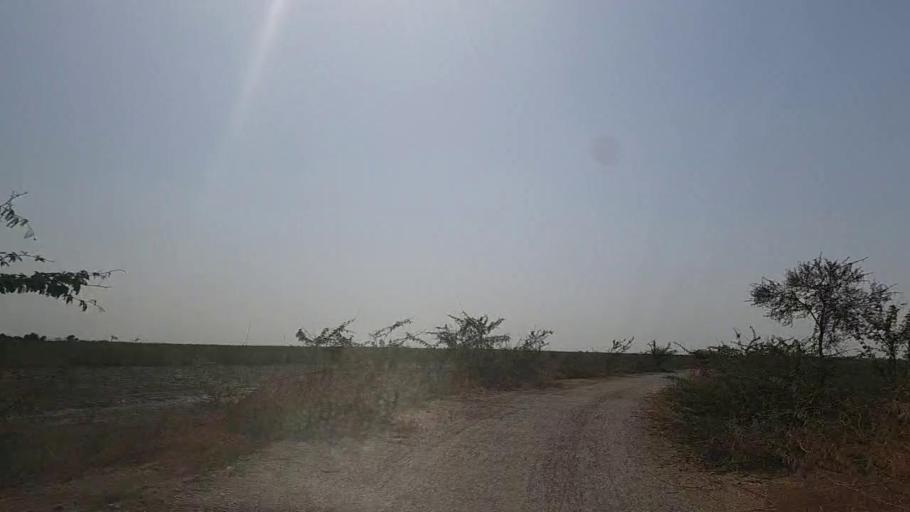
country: PK
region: Sindh
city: Naukot
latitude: 24.5927
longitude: 69.3081
